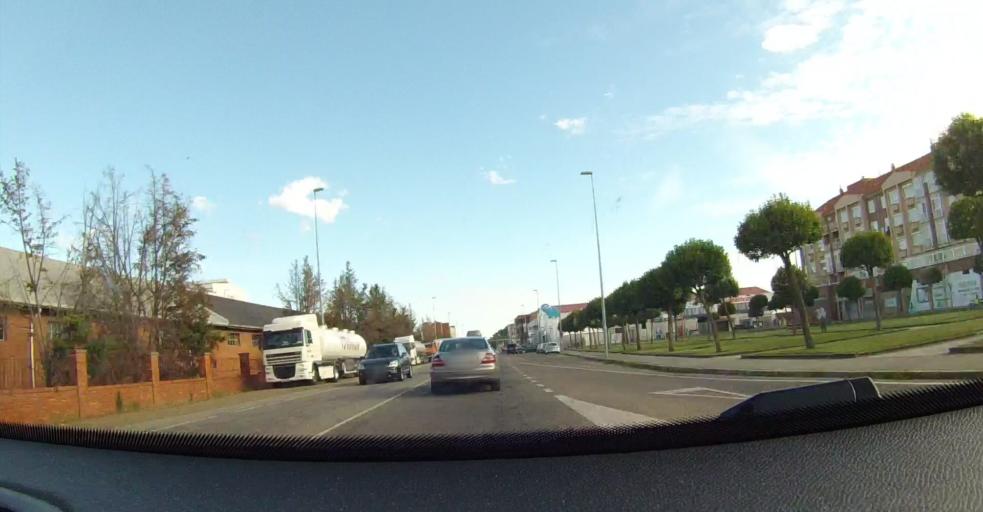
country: ES
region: Castille and Leon
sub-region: Provincia de Leon
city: Leon
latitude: 42.5811
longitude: -5.5838
